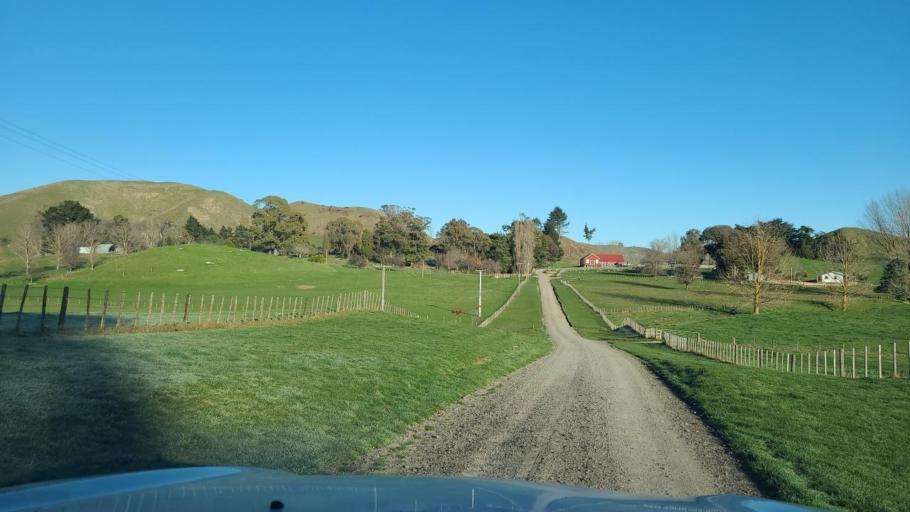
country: NZ
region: Hawke's Bay
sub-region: Hastings District
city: Hastings
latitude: -39.7964
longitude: 176.8204
